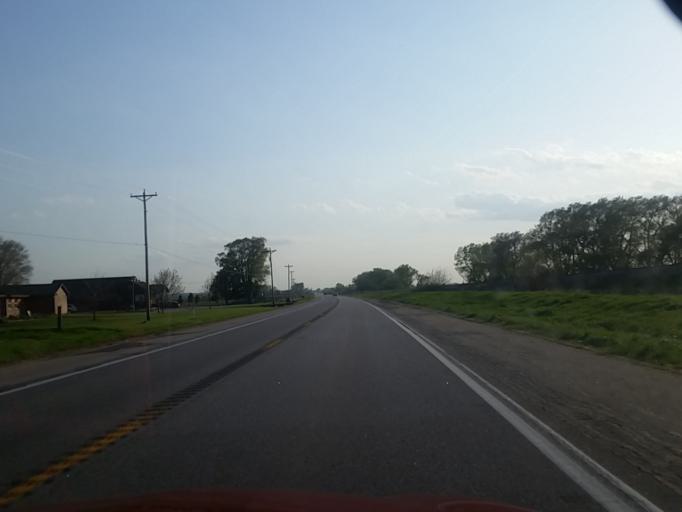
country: US
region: Nebraska
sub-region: Sarpy County
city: Gretna
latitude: 41.0849
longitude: -96.2862
